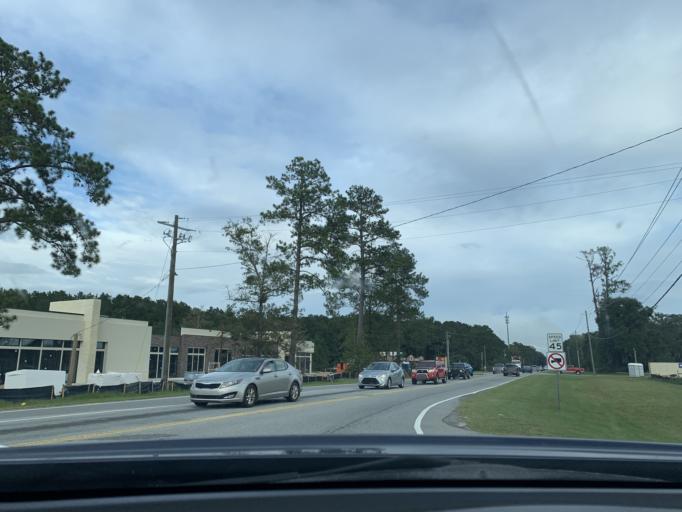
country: US
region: Georgia
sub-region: Chatham County
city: Pooler
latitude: 32.0970
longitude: -81.2719
